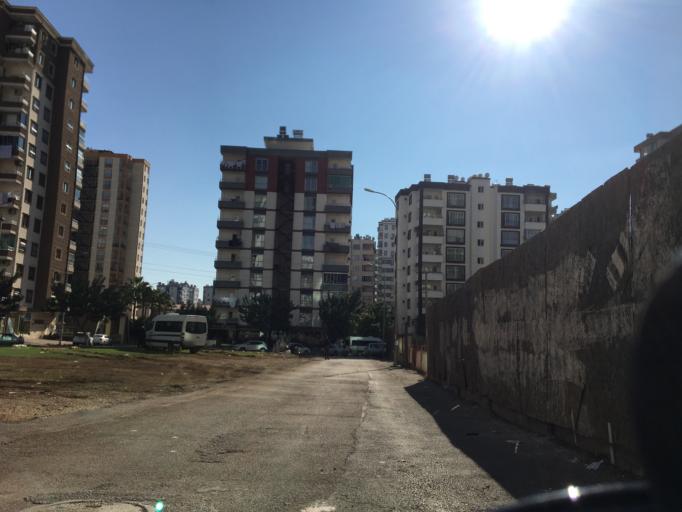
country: TR
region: Adana
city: Seyhan
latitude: 37.0215
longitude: 35.2862
